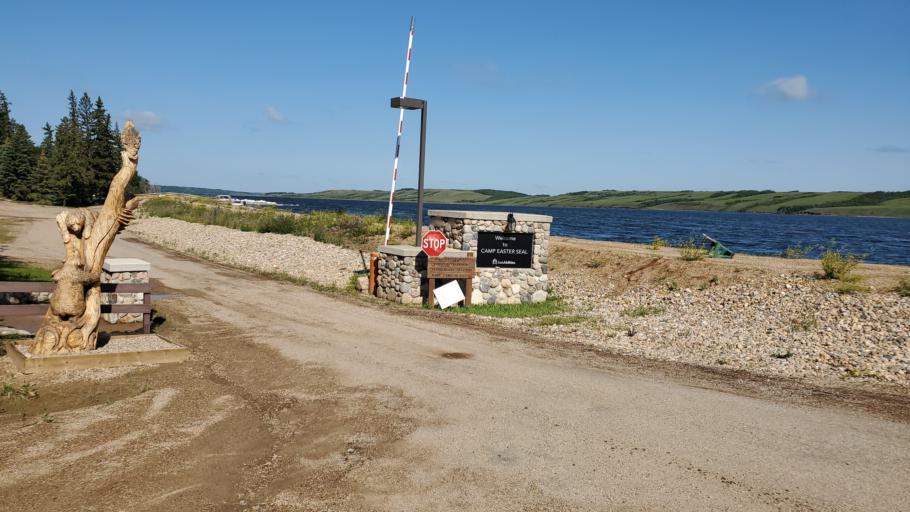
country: CA
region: Saskatchewan
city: Watrous
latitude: 51.7220
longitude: -105.4550
